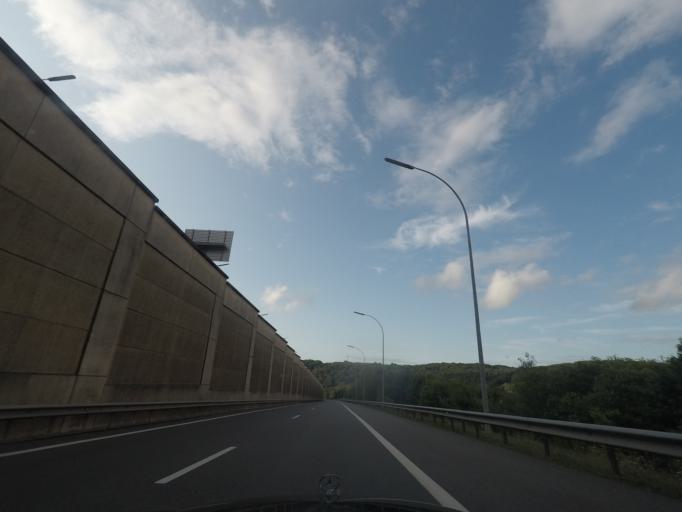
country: LU
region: Luxembourg
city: Colmar
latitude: 49.8058
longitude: 6.1096
